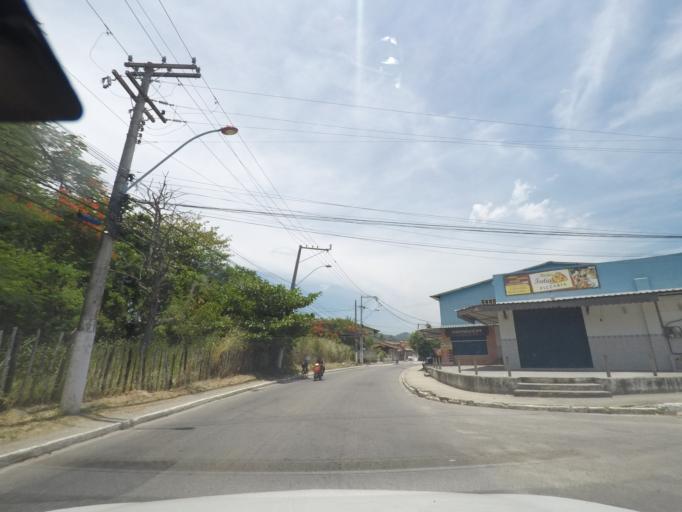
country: BR
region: Rio de Janeiro
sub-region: Marica
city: Marica
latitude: -22.9126
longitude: -42.8235
